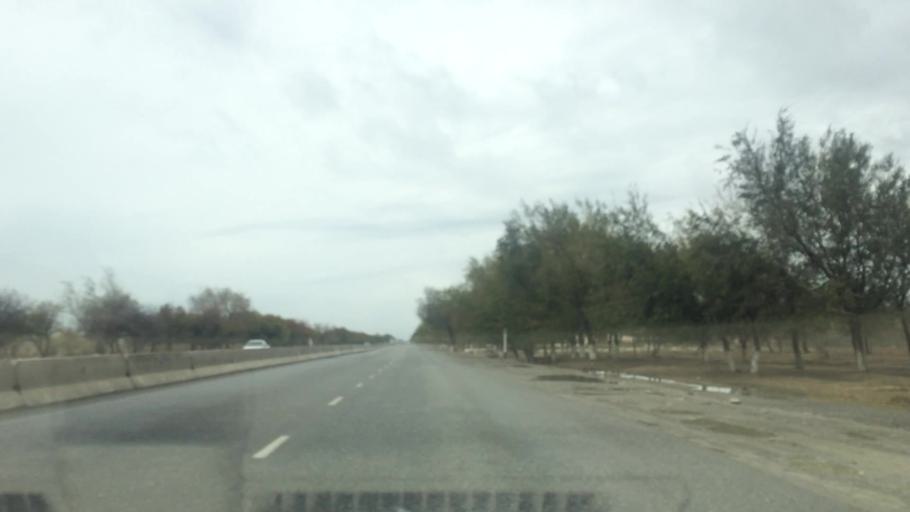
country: UZ
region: Samarqand
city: Bulung'ur
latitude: 39.8370
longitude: 67.4271
